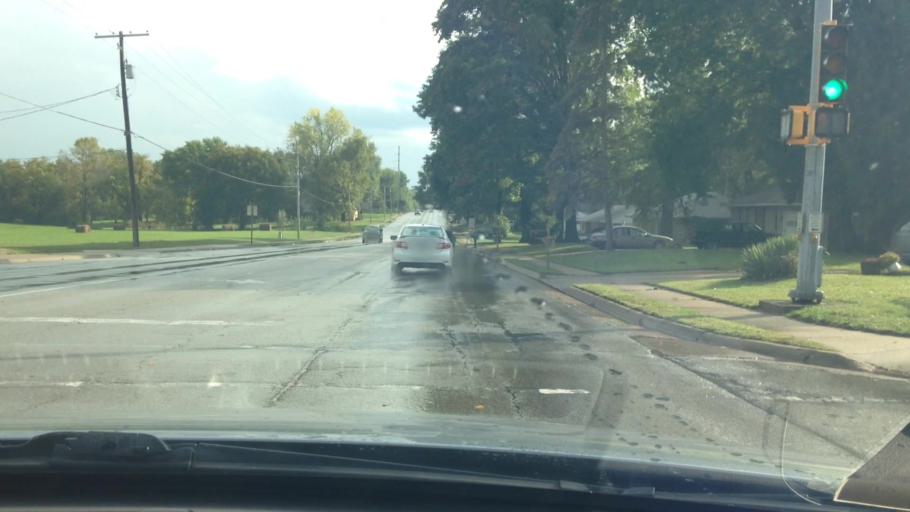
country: US
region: Kansas
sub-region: Leavenworth County
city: Leavenworth
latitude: 39.2886
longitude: -94.9278
